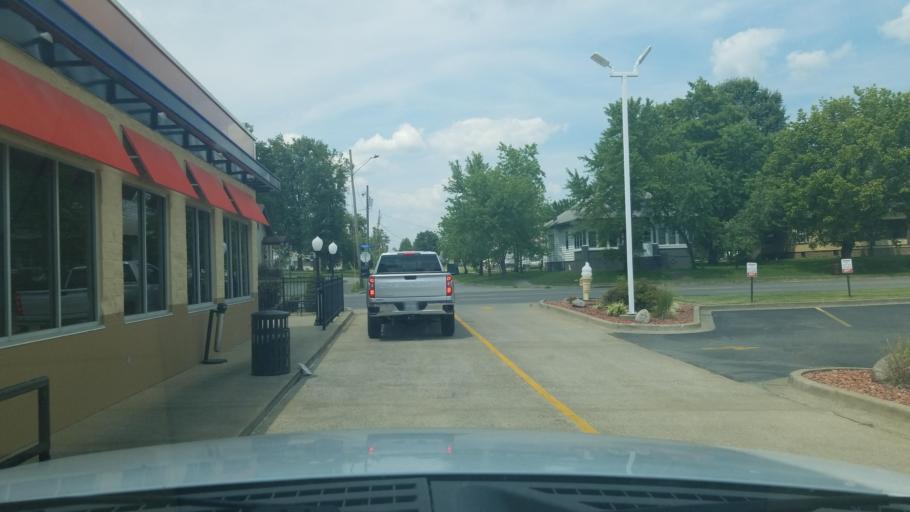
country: US
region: Illinois
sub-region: Williamson County
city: Marion
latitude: 37.7406
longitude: -88.9255
